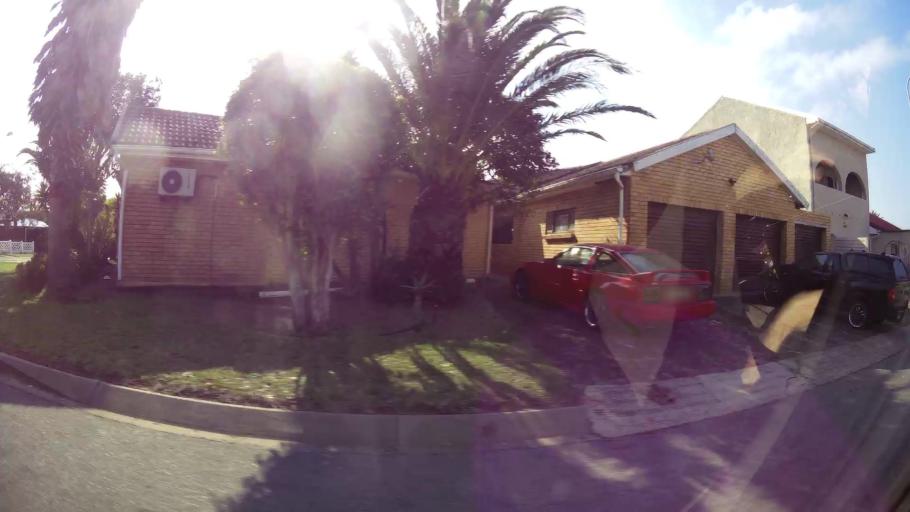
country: ZA
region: Eastern Cape
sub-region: Nelson Mandela Bay Metropolitan Municipality
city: Port Elizabeth
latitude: -33.9246
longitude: 25.5294
